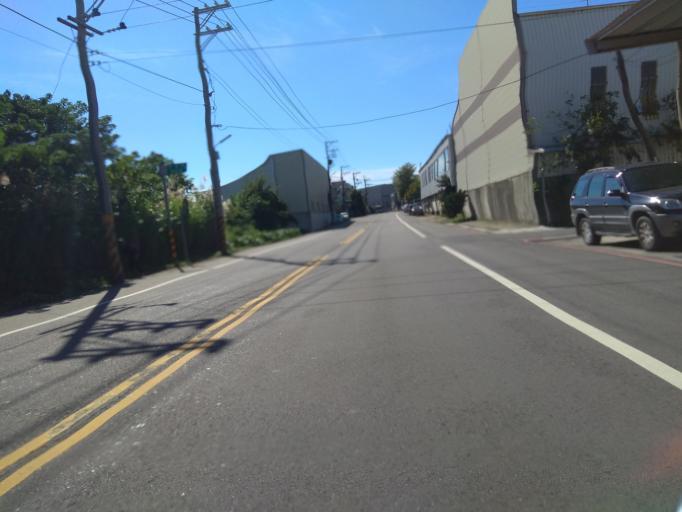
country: TW
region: Taiwan
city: Taoyuan City
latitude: 24.9793
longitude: 121.1365
